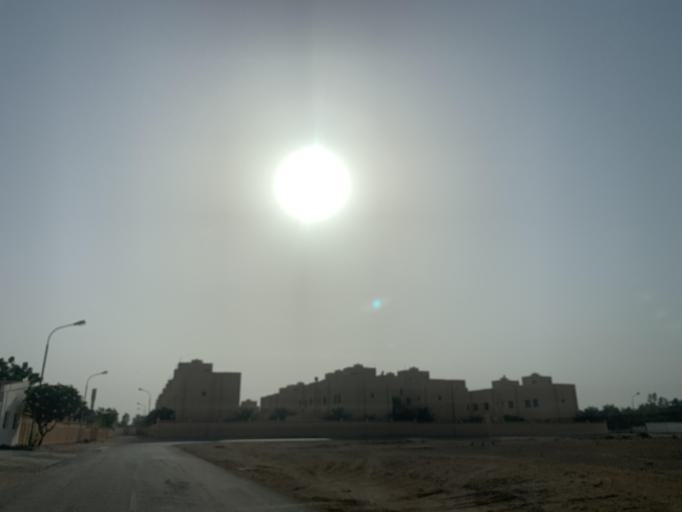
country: BH
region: Central Governorate
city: Madinat Hamad
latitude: 26.1752
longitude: 50.4722
